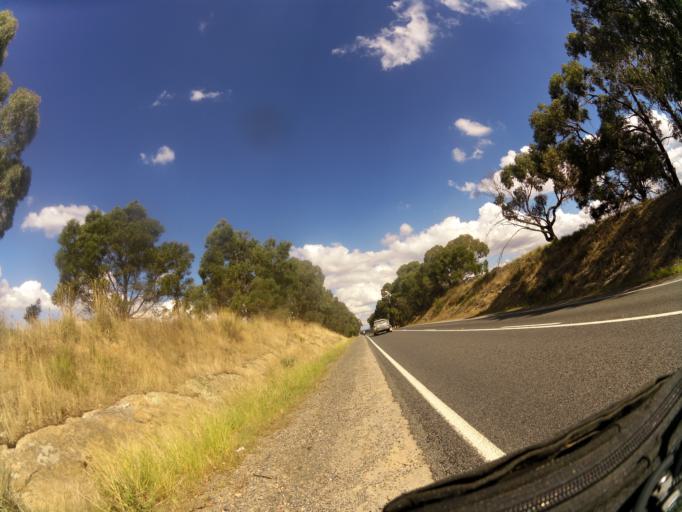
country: AU
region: Victoria
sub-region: Mansfield
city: Mansfield
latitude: -36.8863
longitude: 145.9950
